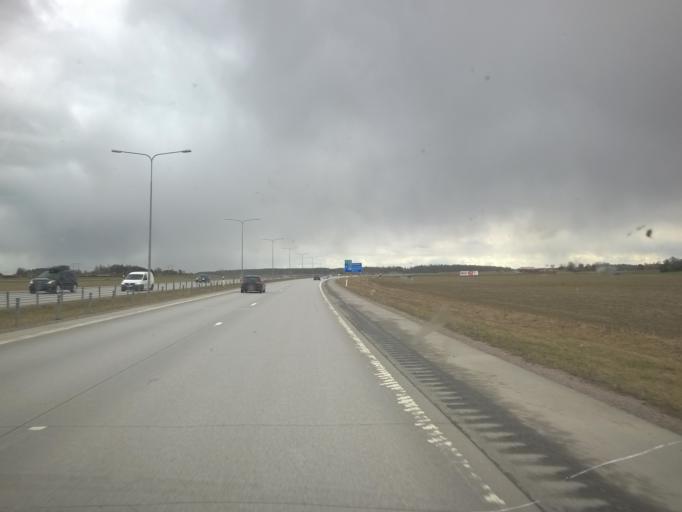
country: SE
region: Uppsala
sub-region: Uppsala Kommun
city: Saevja
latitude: 59.8576
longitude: 17.7291
